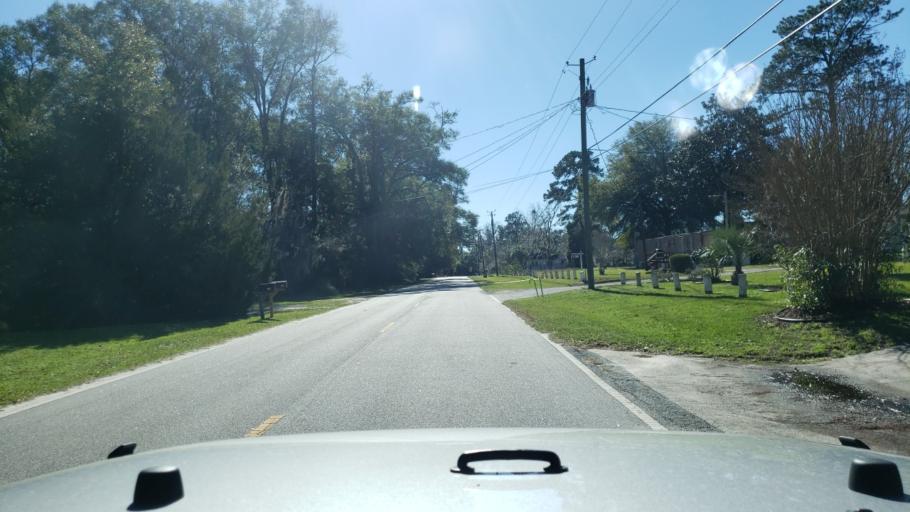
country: US
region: Georgia
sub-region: Chatham County
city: Georgetown
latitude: 32.0361
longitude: -81.1877
